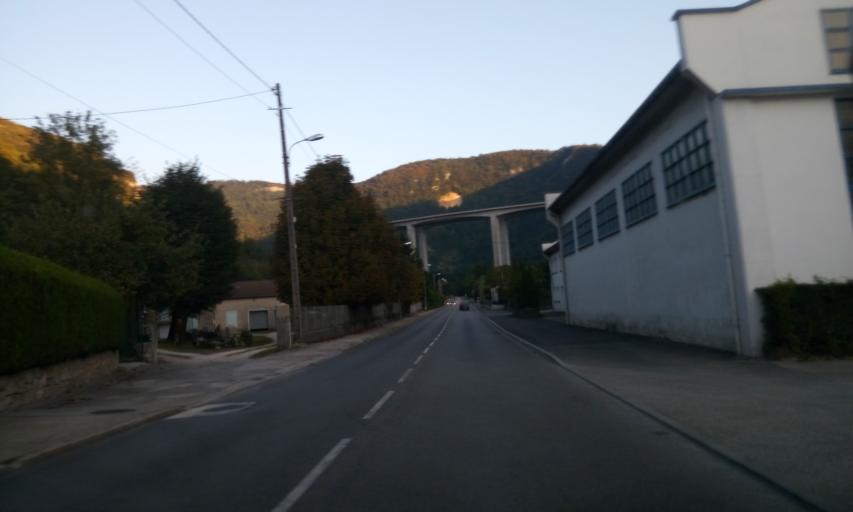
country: FR
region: Rhone-Alpes
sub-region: Departement de l'Ain
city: Nantua
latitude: 46.1469
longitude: 5.6112
